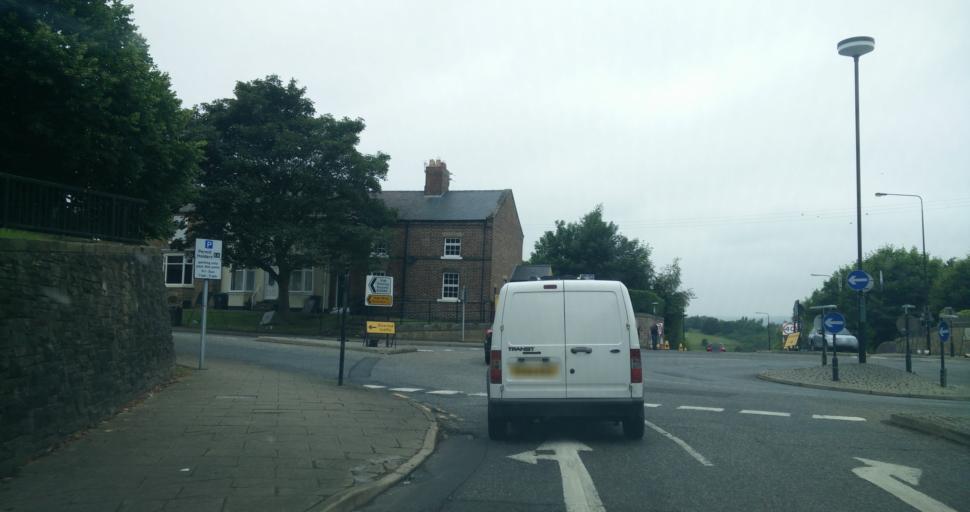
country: GB
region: England
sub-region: County Durham
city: Bishop Auckland
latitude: 54.6645
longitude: -1.6798
